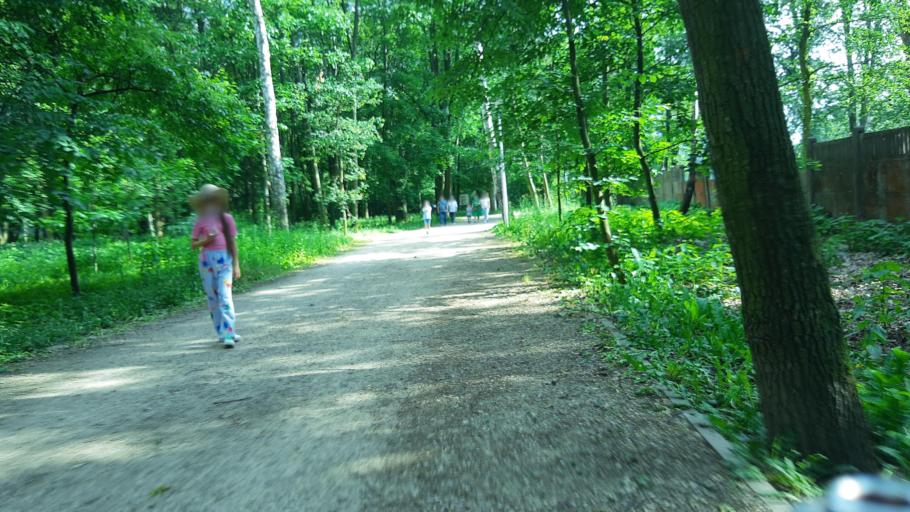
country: PL
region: Lodz Voivodeship
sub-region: Powiat sieradzki
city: Sieradz
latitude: 51.5972
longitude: 18.7535
